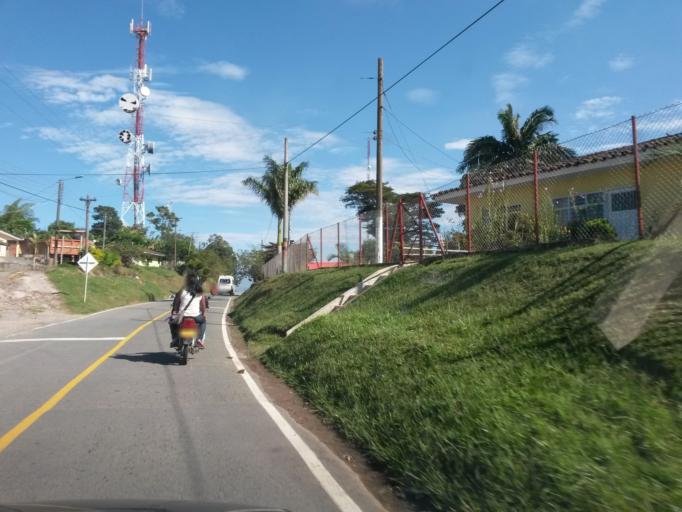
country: CO
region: Cauca
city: Morales
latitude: 2.7495
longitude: -76.6257
